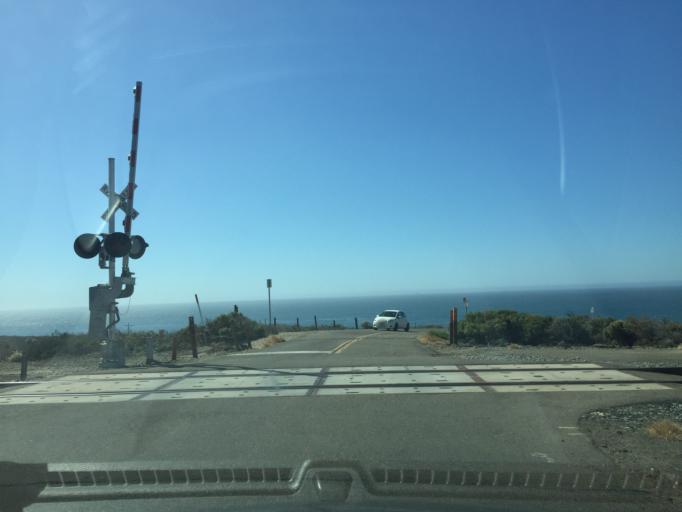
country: US
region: California
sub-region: Santa Barbara County
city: Lompoc
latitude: 34.5019
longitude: -120.4965
